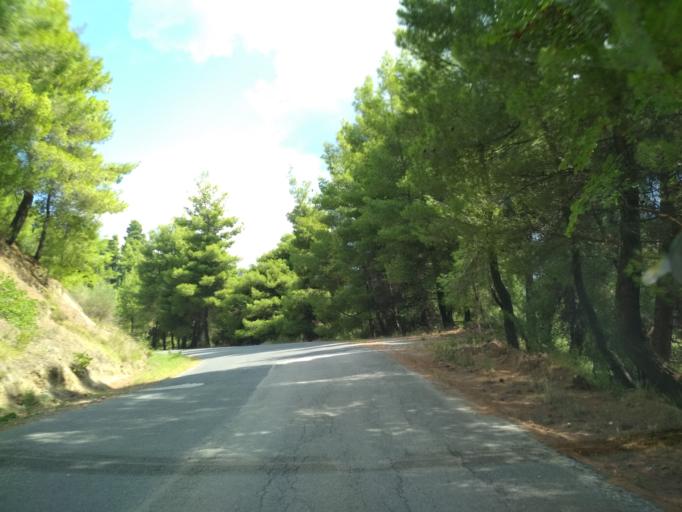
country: GR
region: Central Greece
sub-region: Nomos Evvoias
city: Roviai
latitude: 38.8332
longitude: 23.2845
